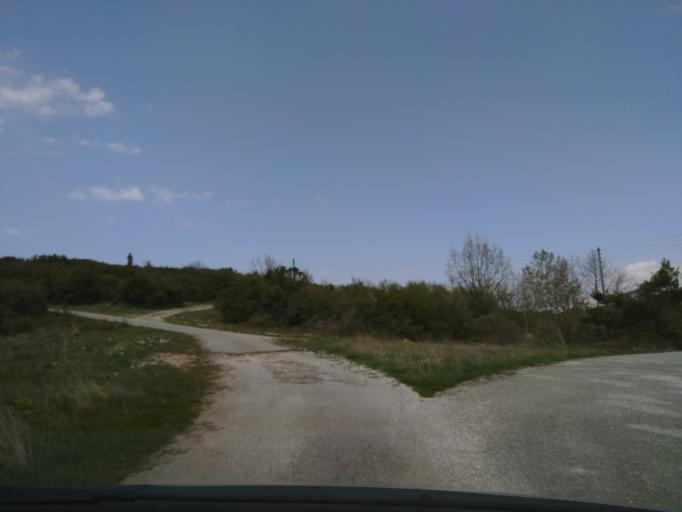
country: GR
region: Epirus
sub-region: Nomos Ioanninon
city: Asprangeloi
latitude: 39.8375
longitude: 20.7049
